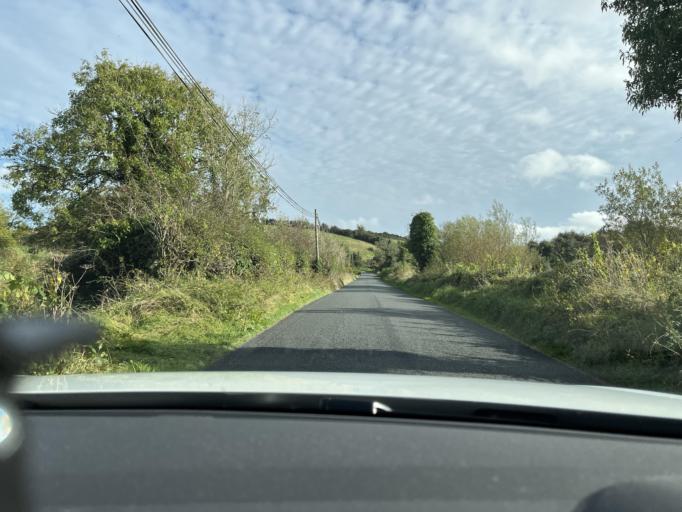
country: IE
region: Connaught
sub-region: Sligo
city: Ballymote
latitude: 54.0832
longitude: -8.4434
